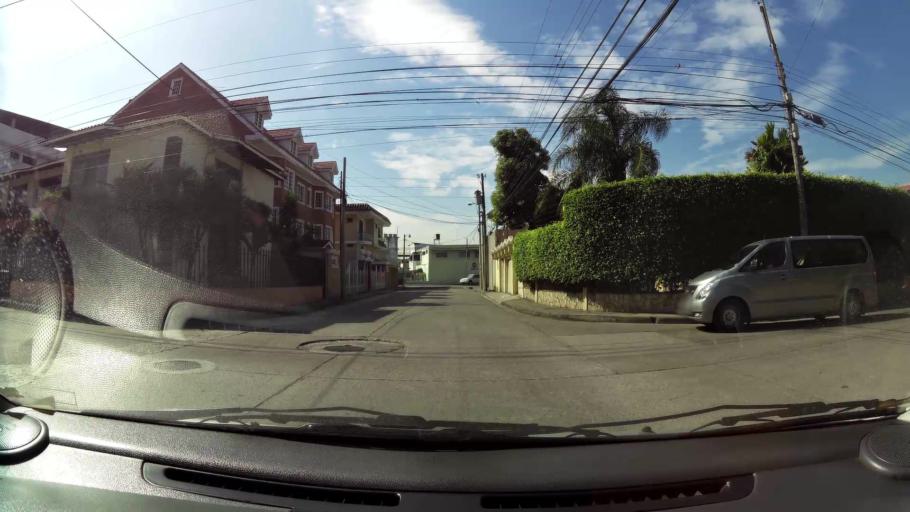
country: EC
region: Guayas
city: Guayaquil
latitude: -2.2292
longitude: -79.8942
